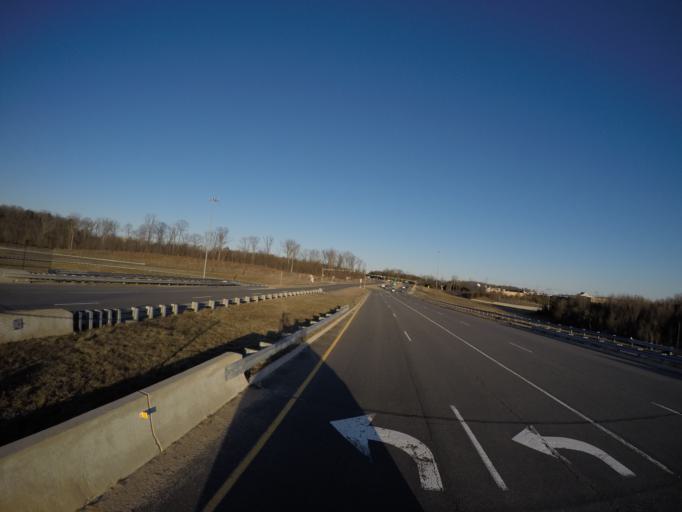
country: US
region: Virginia
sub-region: Loudoun County
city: Dulles Town Center
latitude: 39.0277
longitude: -77.4309
